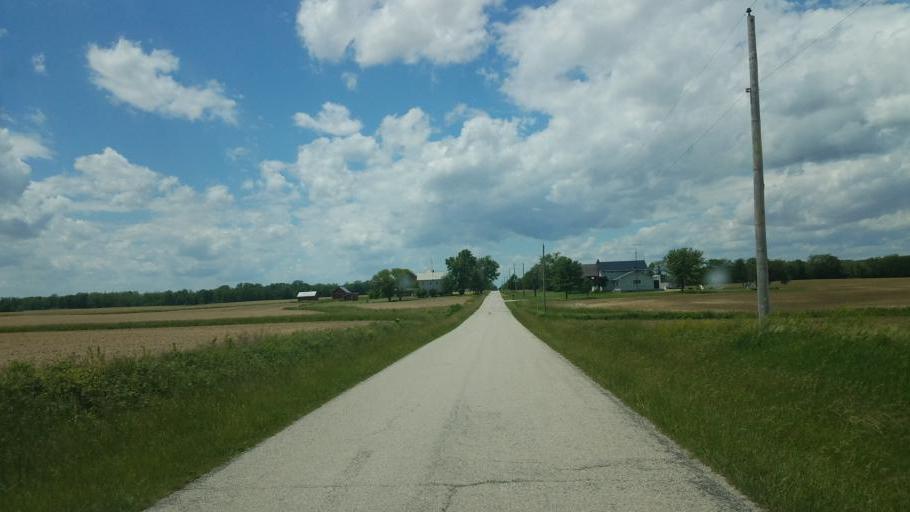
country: US
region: Ohio
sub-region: Huron County
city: Willard
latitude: 41.1426
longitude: -82.7663
